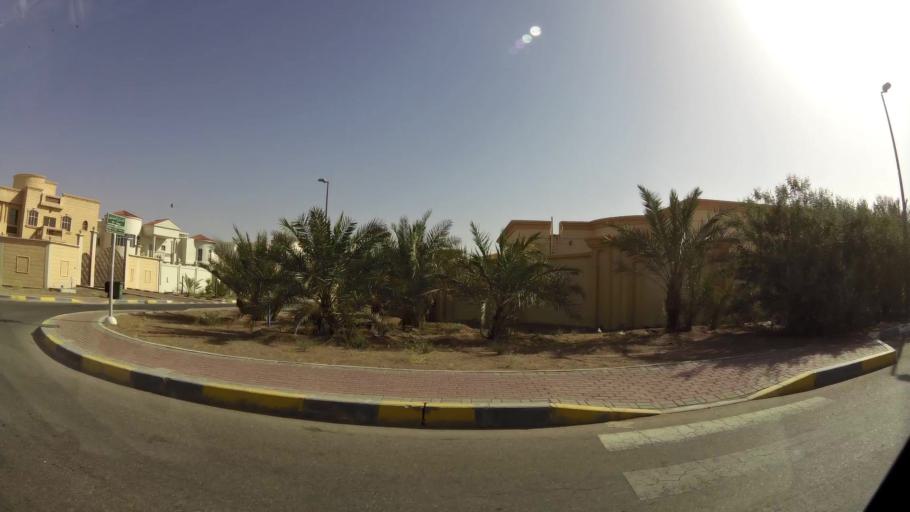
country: OM
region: Al Buraimi
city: Al Buraymi
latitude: 24.3471
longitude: 55.7982
